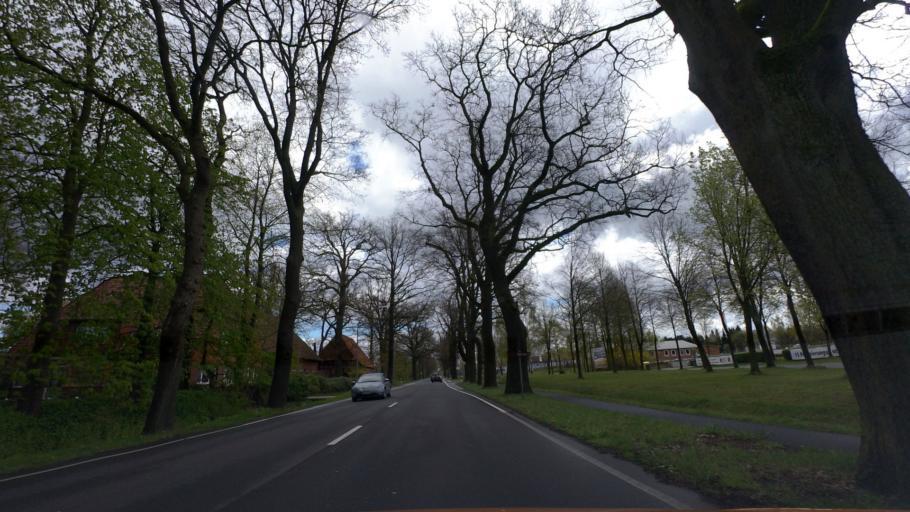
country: DE
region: Lower Saxony
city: Sottrum
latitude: 53.1147
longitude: 9.2412
